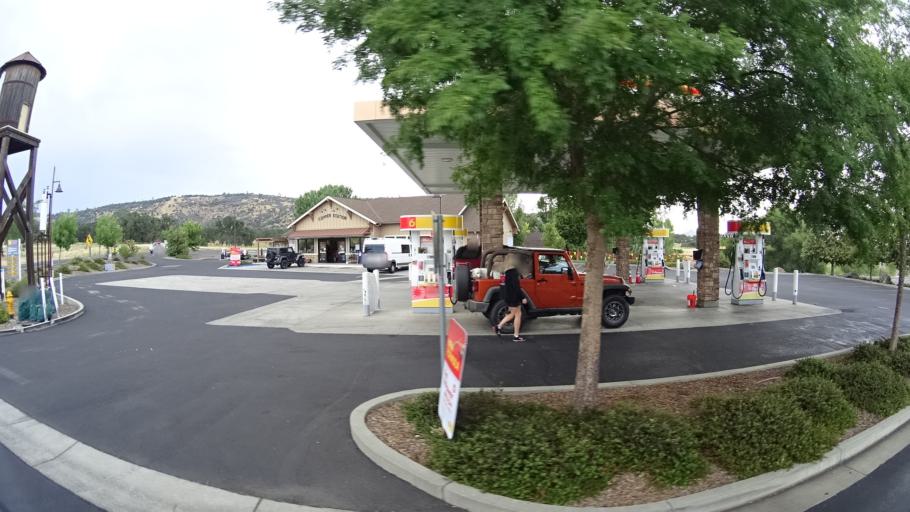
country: US
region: California
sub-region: Calaveras County
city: Copperopolis
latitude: 37.9730
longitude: -120.6516
